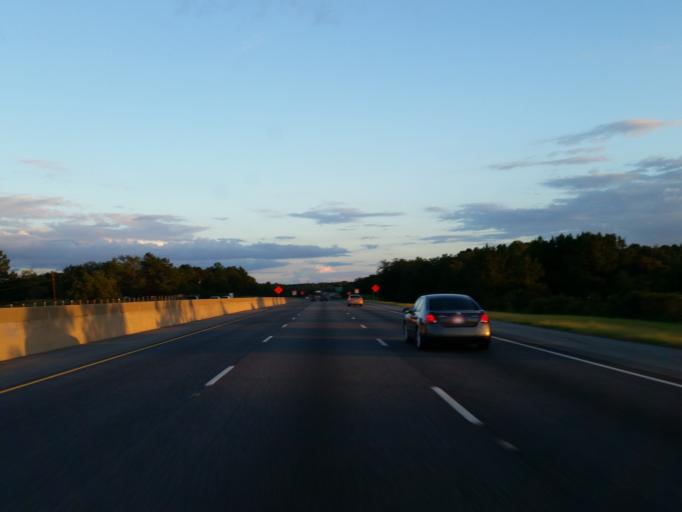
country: US
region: Georgia
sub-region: Tift County
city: Tifton
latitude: 31.5268
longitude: -83.5219
